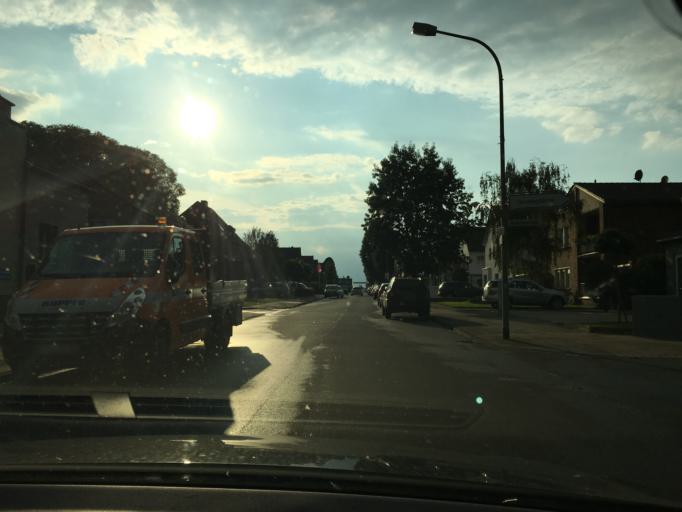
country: DE
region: North Rhine-Westphalia
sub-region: Regierungsbezirk Koln
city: Norvenich
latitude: 50.8094
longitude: 6.6416
